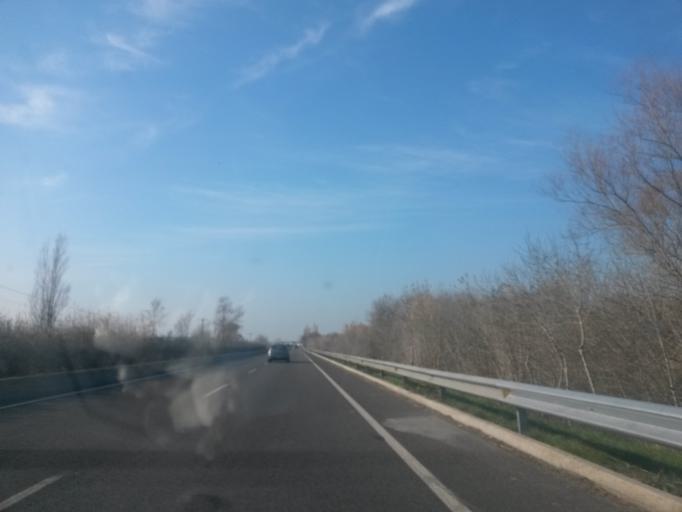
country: ES
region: Catalonia
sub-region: Provincia de Girona
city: Empuriabrava
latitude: 42.2652
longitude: 3.1184
